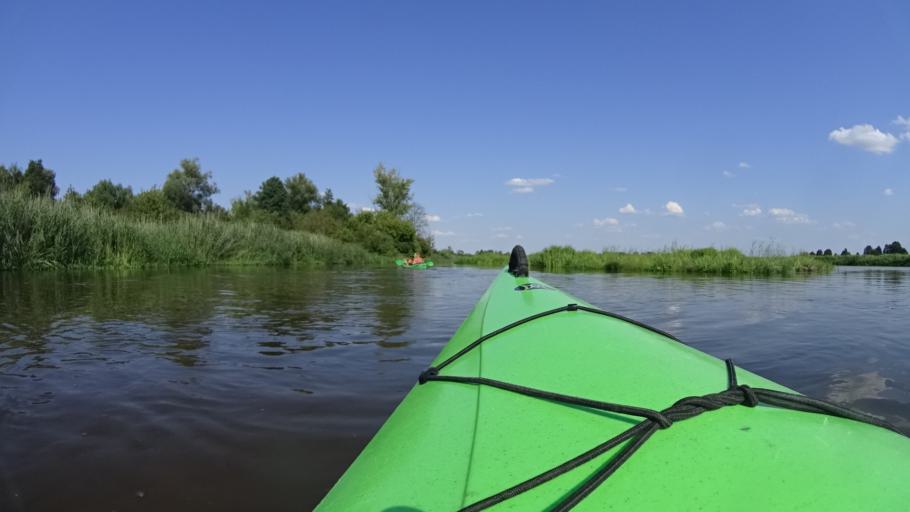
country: PL
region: Masovian Voivodeship
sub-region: Powiat bialobrzeski
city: Bialobrzegi
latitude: 51.6618
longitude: 20.9320
